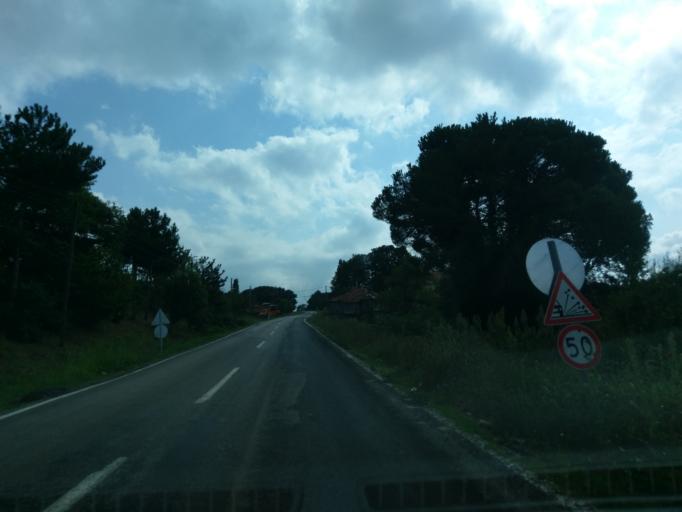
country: TR
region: Sinop
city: Erfelek
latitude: 41.9465
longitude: 34.7876
